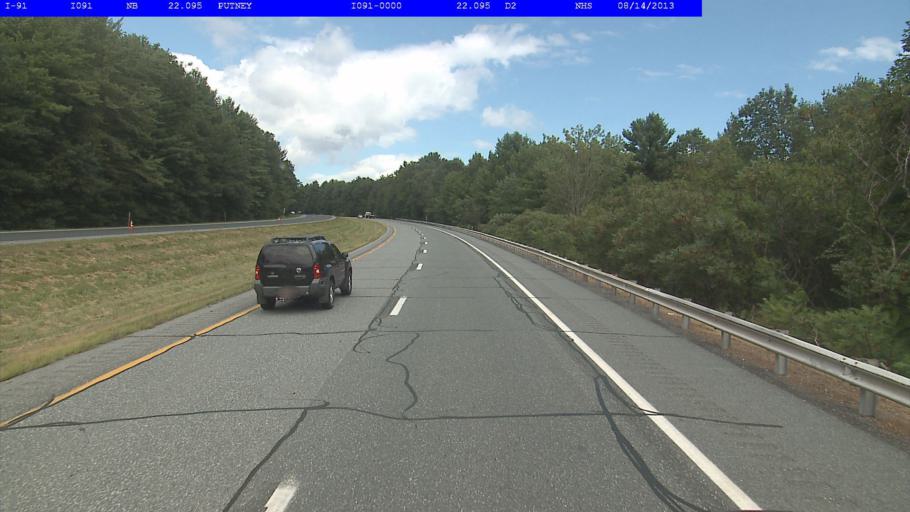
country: US
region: New Hampshire
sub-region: Cheshire County
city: Westmoreland
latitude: 42.9999
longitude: -72.4689
